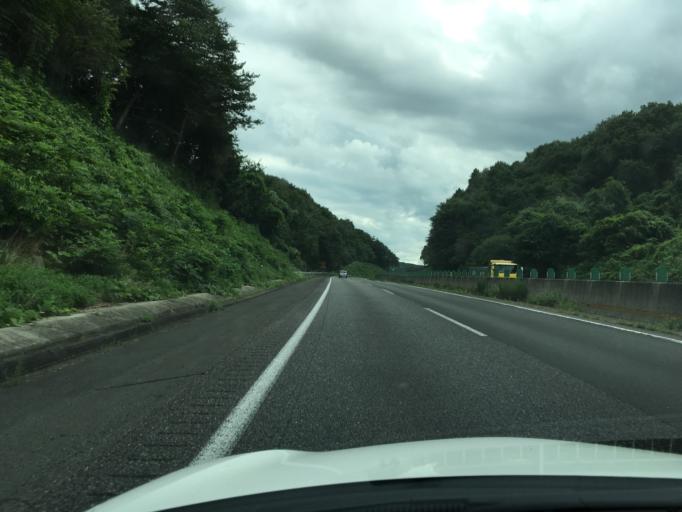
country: JP
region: Fukushima
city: Nihommatsu
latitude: 37.6277
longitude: 140.4319
